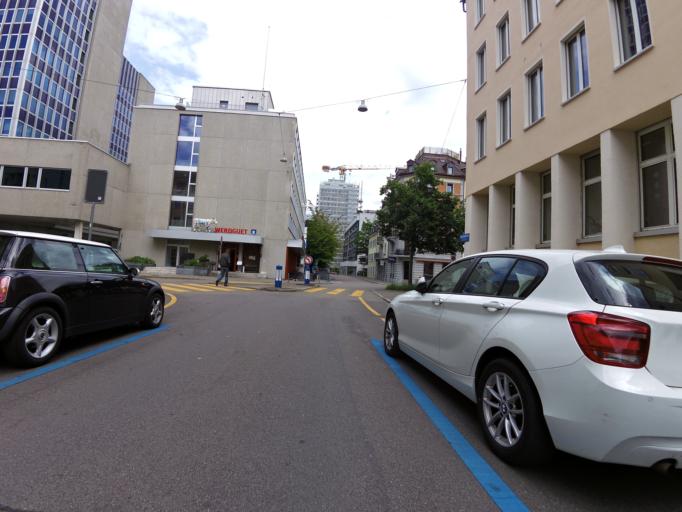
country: CH
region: Zurich
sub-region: Bezirk Zuerich
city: Zuerich (Kreis 4) / Werd
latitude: 47.3712
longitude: 8.5272
